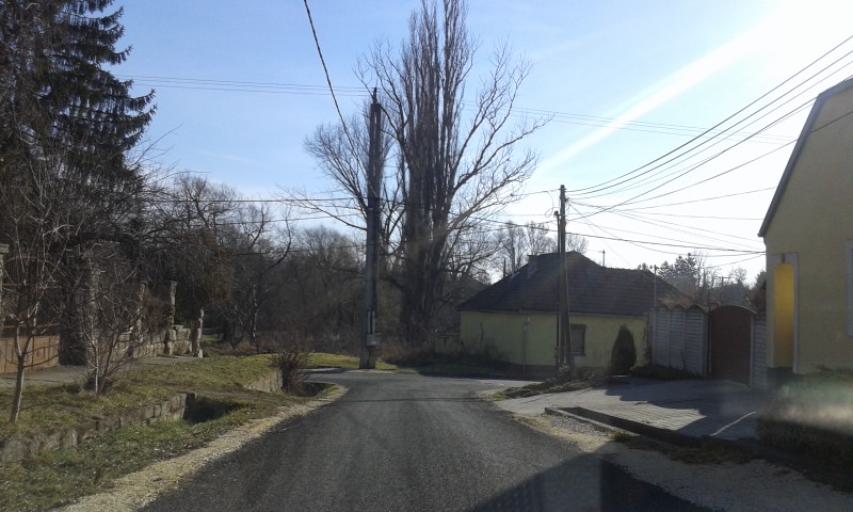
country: HU
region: Pest
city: Soskut
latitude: 47.4029
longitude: 18.8213
